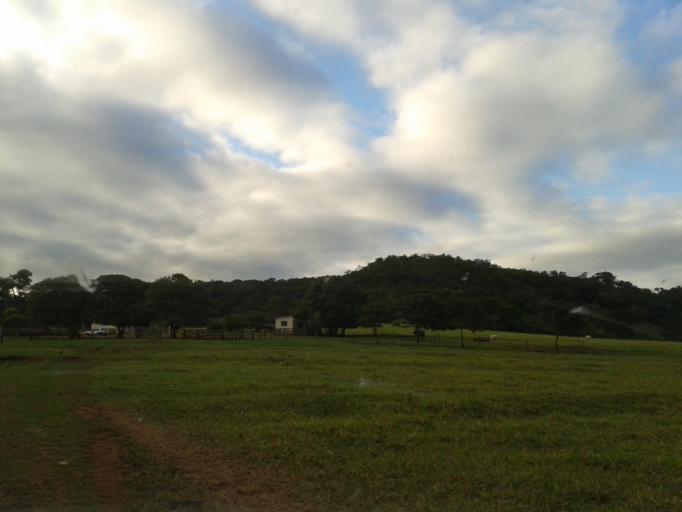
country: BR
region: Minas Gerais
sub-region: Campina Verde
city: Campina Verde
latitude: -19.4601
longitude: -49.6483
